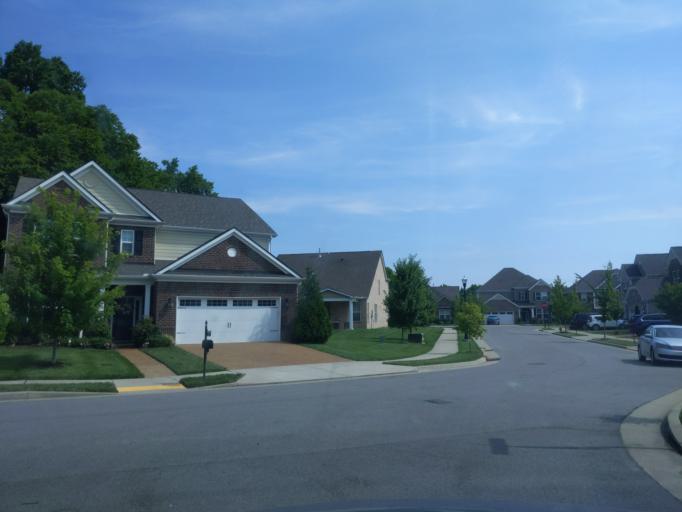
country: US
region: Tennessee
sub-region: Williamson County
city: Brentwood Estates
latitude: 36.0294
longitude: -86.7483
